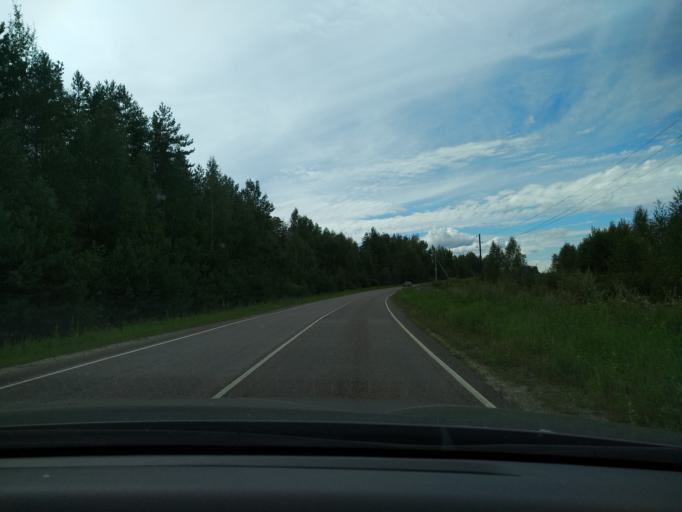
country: RU
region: Moskovskaya
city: Krasnyy Tkach
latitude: 55.3812
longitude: 39.1907
